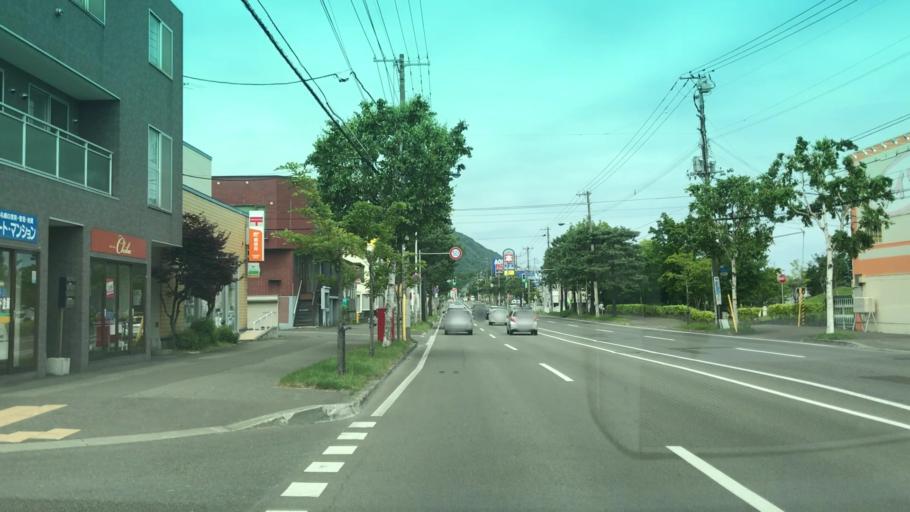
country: JP
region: Hokkaido
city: Sapporo
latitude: 43.0731
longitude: 141.2802
